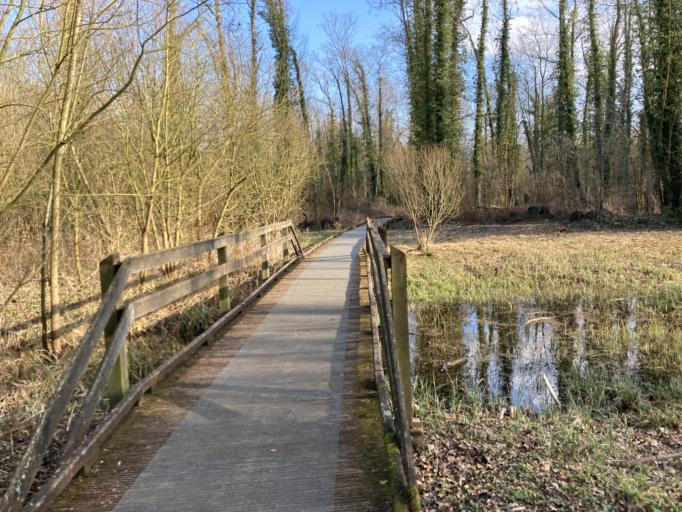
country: FR
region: Nord-Pas-de-Calais
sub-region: Departement du Pas-de-Calais
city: Annequin
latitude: 50.5217
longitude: 2.7094
